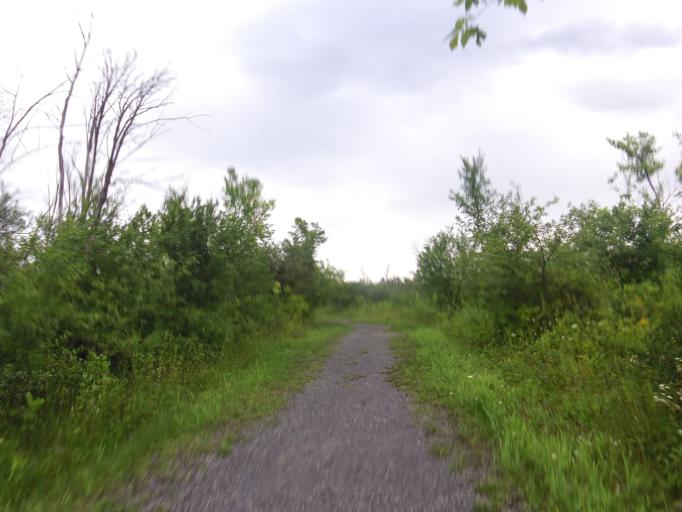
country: CA
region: Ontario
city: Bells Corners
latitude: 45.3578
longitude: -75.8605
